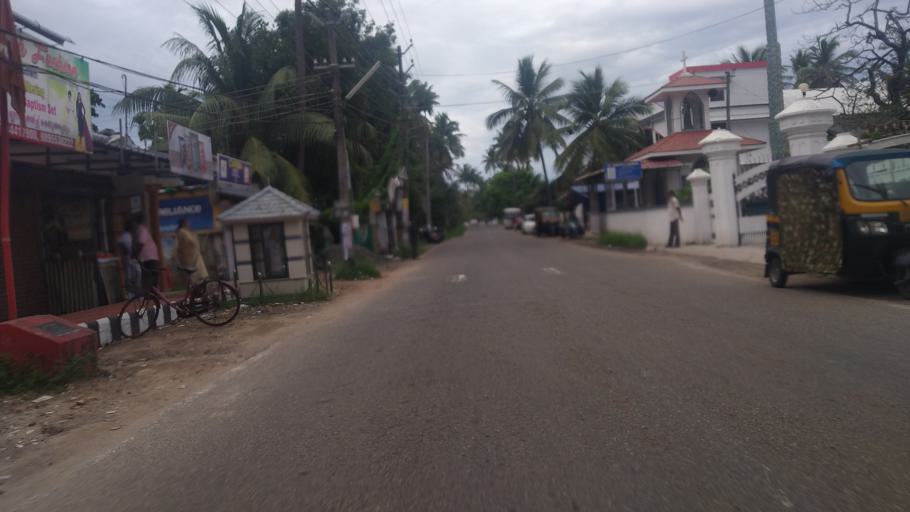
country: IN
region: Kerala
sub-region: Ernakulam
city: Cochin
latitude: 9.8935
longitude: 76.2590
